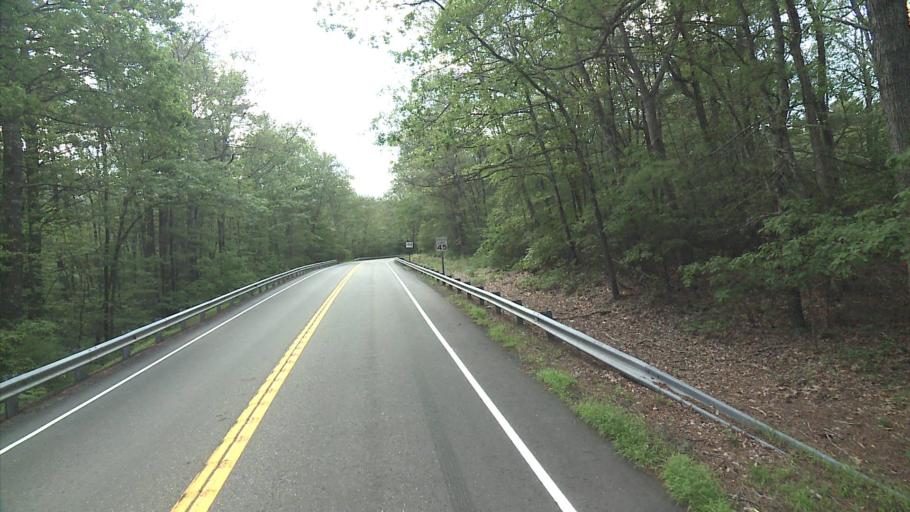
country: US
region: Massachusetts
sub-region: Worcester County
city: Southbridge
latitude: 42.0273
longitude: -72.0719
